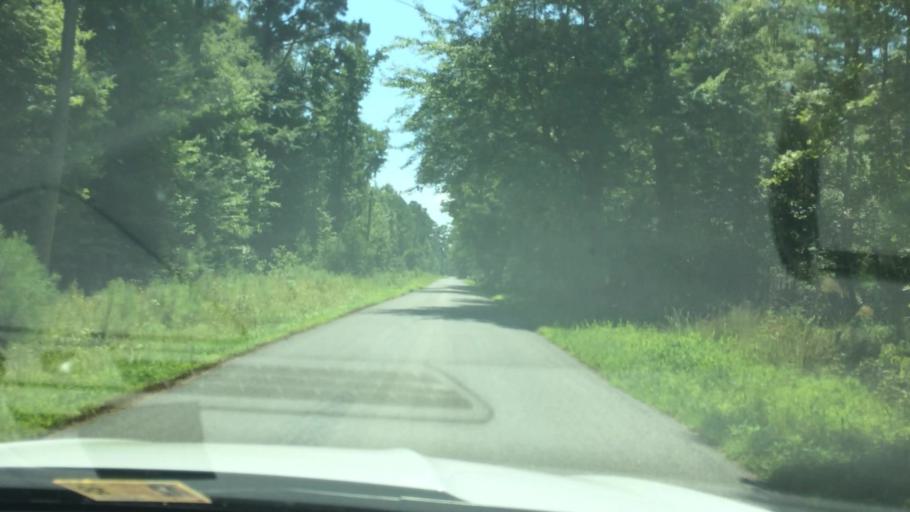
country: US
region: Virginia
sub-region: Charles City County
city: Charles City
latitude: 37.2980
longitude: -76.9656
